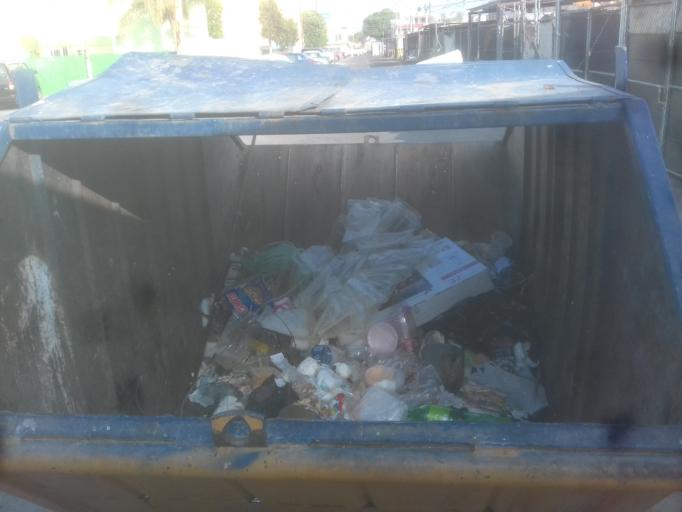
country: MX
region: Aguascalientes
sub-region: Aguascalientes
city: Aguascalientes
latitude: 21.8664
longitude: -102.2756
